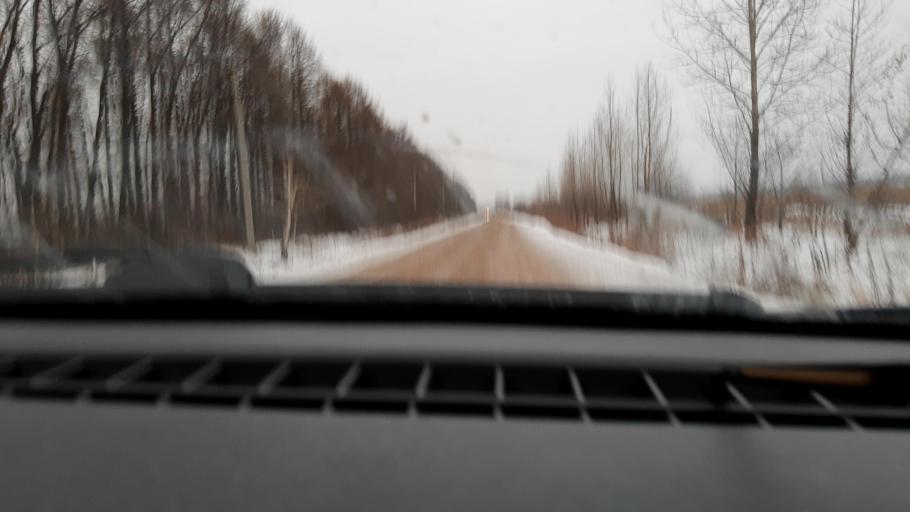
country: RU
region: Bashkortostan
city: Iglino
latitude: 54.7336
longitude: 56.2545
